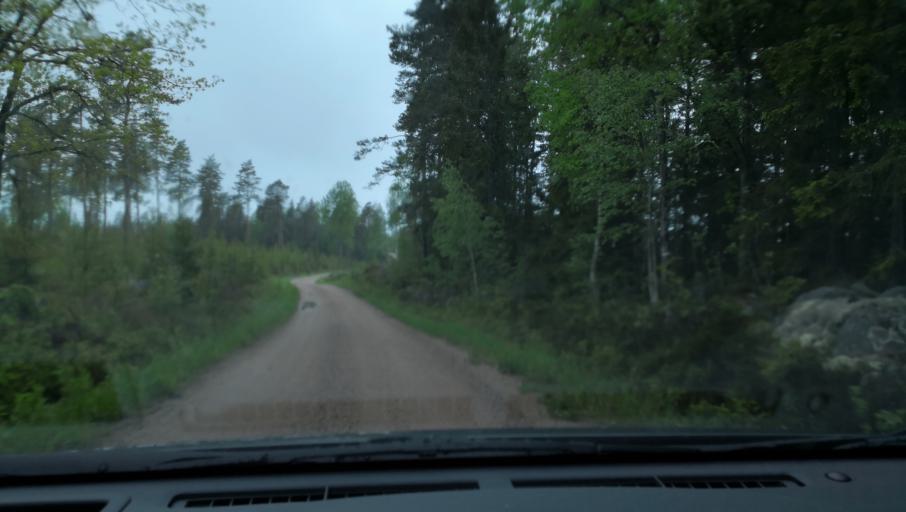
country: SE
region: Uppsala
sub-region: Enkopings Kommun
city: Orsundsbro
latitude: 59.9303
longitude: 17.3298
